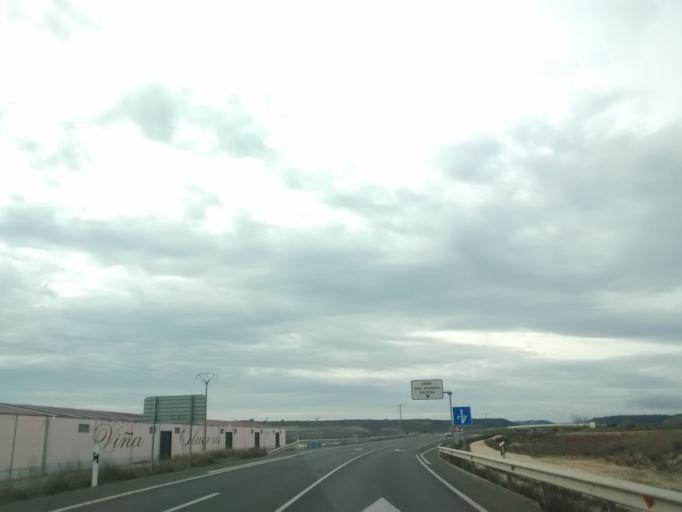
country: ES
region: La Rioja
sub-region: Provincia de La Rioja
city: San Asensio
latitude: 42.5115
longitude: -2.7346
